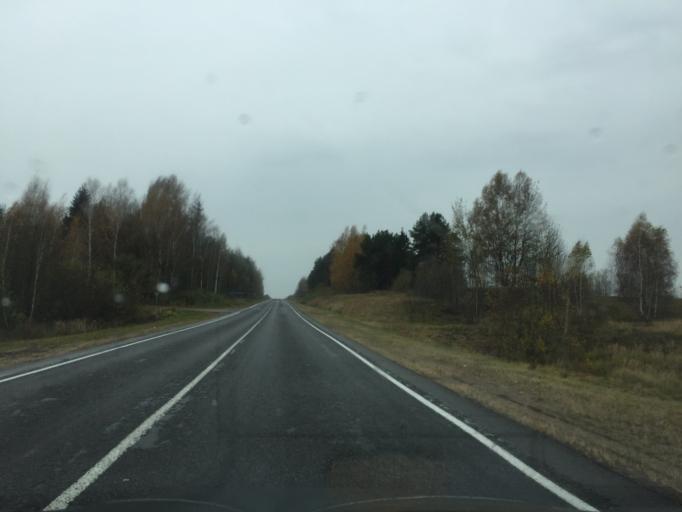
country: BY
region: Gomel
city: Karma
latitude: 53.3111
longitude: 30.7434
